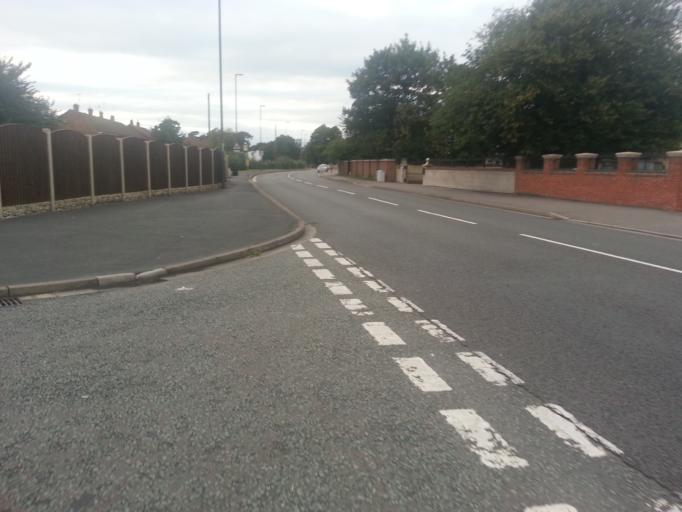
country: GB
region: England
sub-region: Derbyshire
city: Borrowash
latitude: 52.8905
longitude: -1.4203
